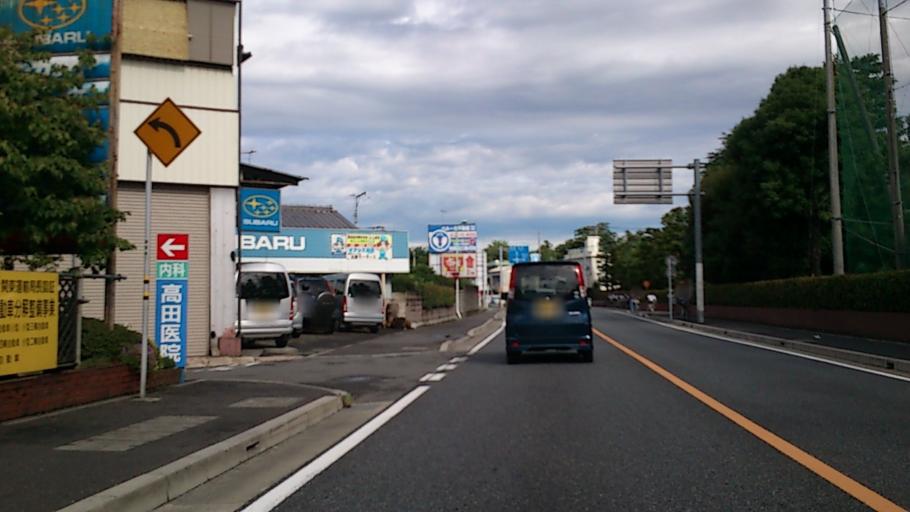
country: JP
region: Saitama
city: Fukayacho
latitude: 36.1962
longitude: 139.2921
